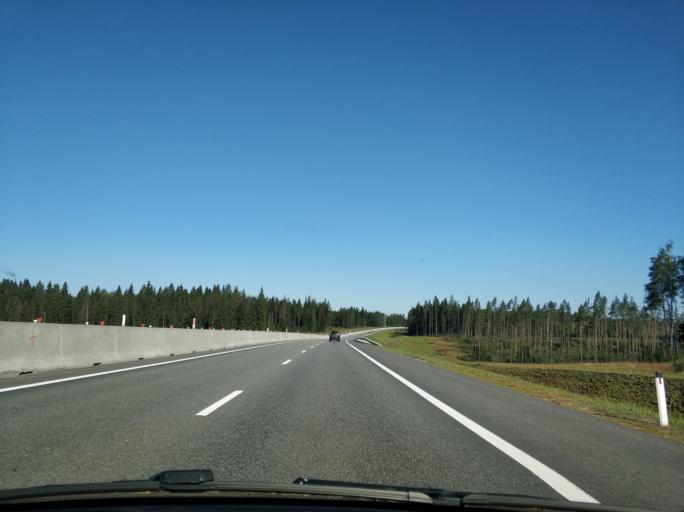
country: RU
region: Leningrad
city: Sosnovo
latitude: 60.5174
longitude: 30.1788
